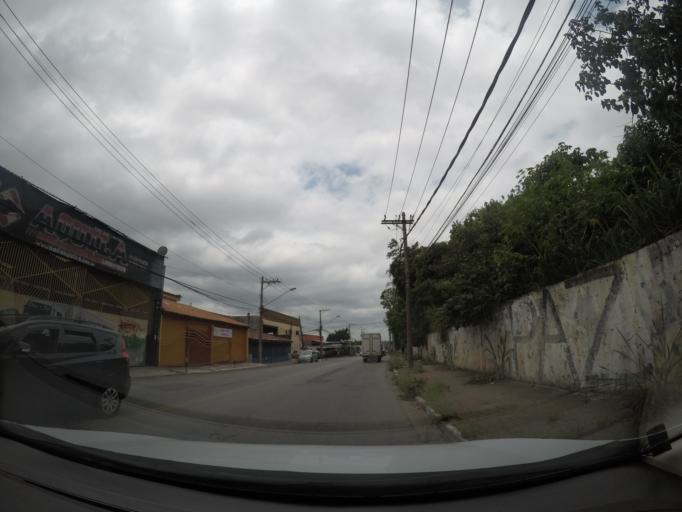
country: BR
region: Sao Paulo
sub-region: Itaquaquecetuba
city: Itaquaquecetuba
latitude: -23.4248
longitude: -46.4266
